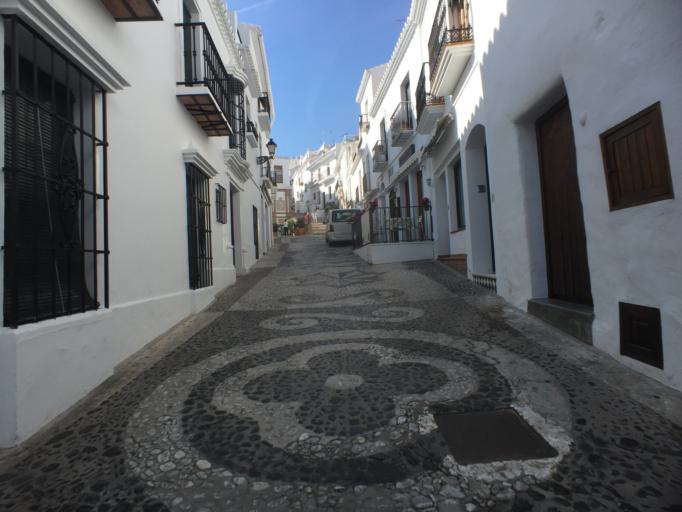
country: ES
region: Andalusia
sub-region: Provincia de Malaga
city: Frigiliana
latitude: 36.7916
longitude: -3.8957
